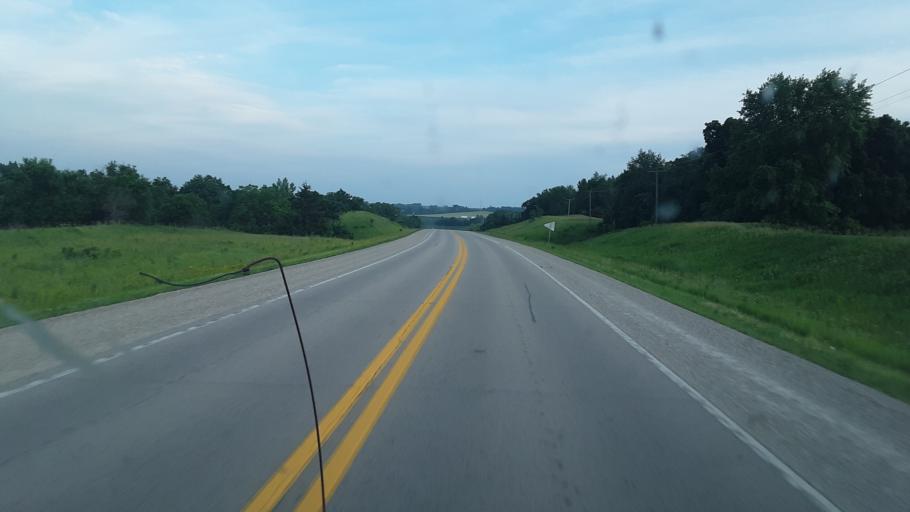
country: US
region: Iowa
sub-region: Benton County
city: Belle Plaine
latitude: 41.7536
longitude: -92.2788
